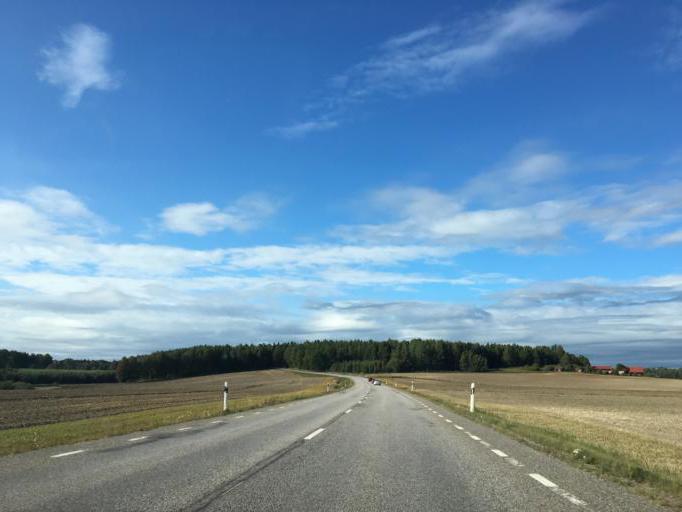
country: SE
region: Soedermanland
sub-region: Nykopings Kommun
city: Svalsta
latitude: 58.8600
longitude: 16.9152
